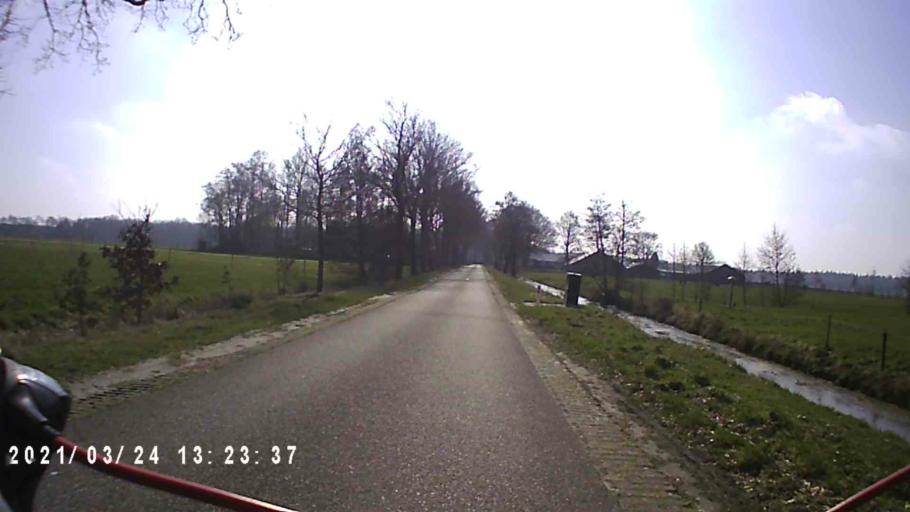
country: NL
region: Groningen
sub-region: Gemeente Grootegast
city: Grootegast
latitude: 53.0987
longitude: 6.2765
